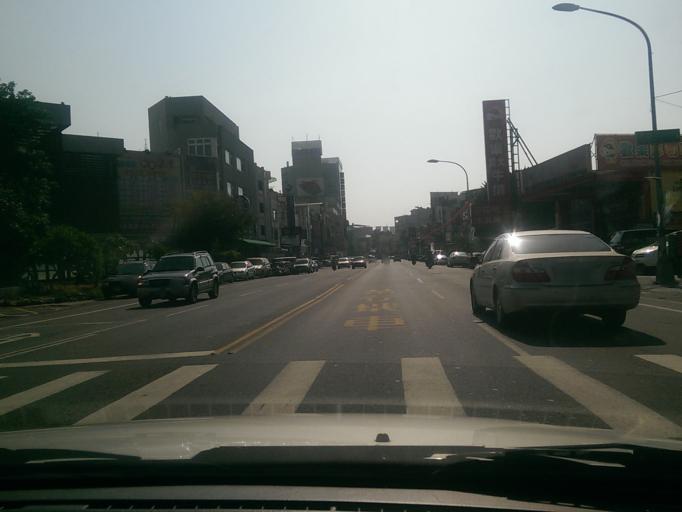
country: TW
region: Taiwan
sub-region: Changhua
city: Chang-hua
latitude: 24.0685
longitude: 120.5403
